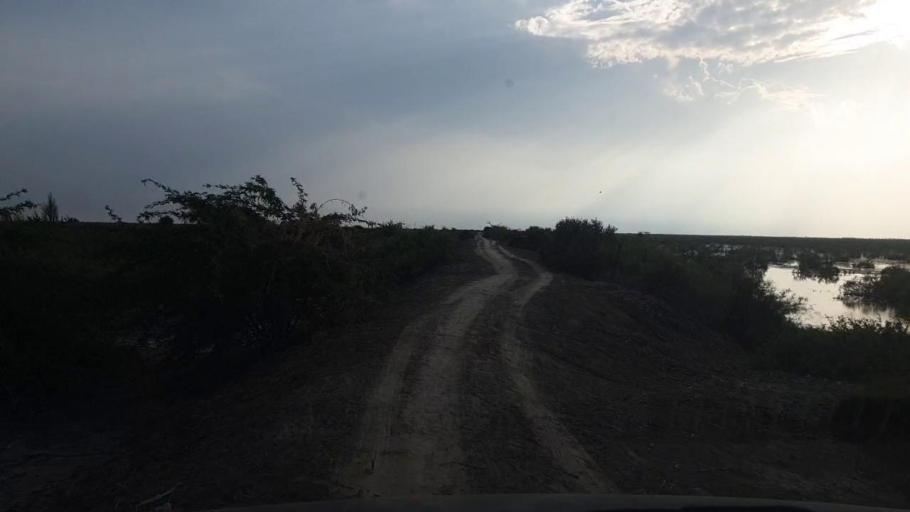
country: PK
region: Sindh
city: Badin
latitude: 24.4379
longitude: 68.6738
